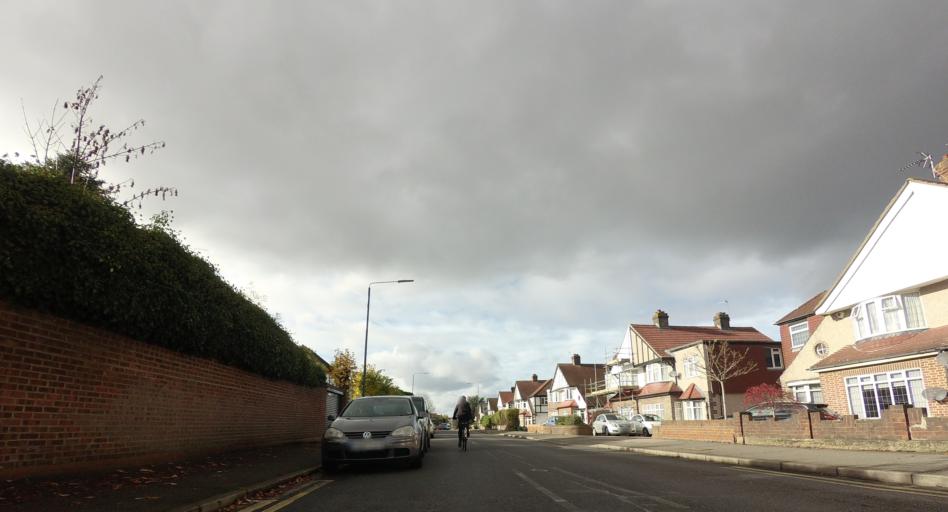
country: GB
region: England
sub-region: Greater London
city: Sidcup
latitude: 51.4343
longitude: 0.1153
